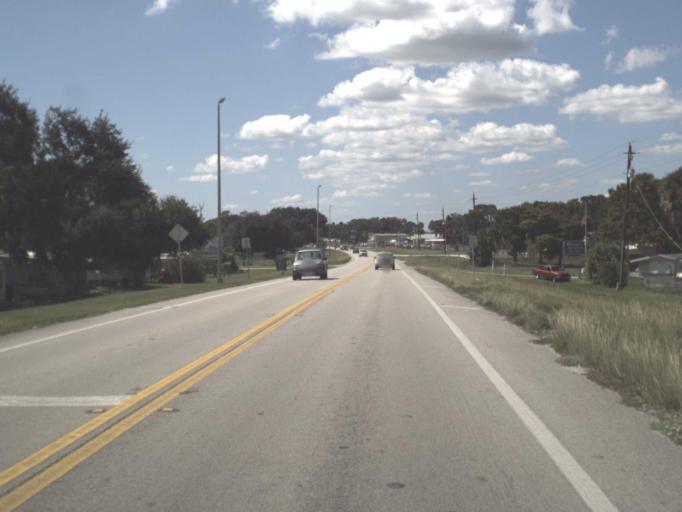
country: US
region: Florida
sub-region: Okeechobee County
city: Taylor Creek
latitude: 27.2100
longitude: -80.7990
